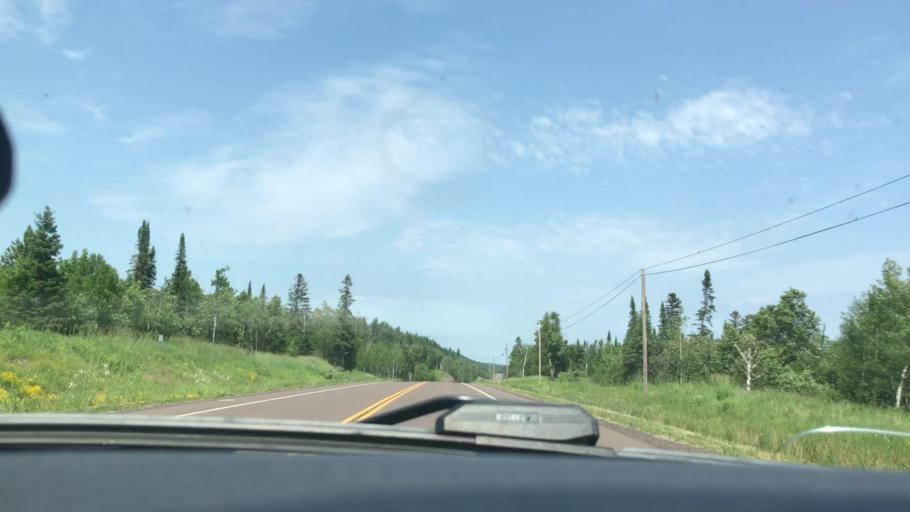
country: US
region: Minnesota
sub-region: Lake County
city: Silver Bay
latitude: 47.4313
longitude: -91.0857
